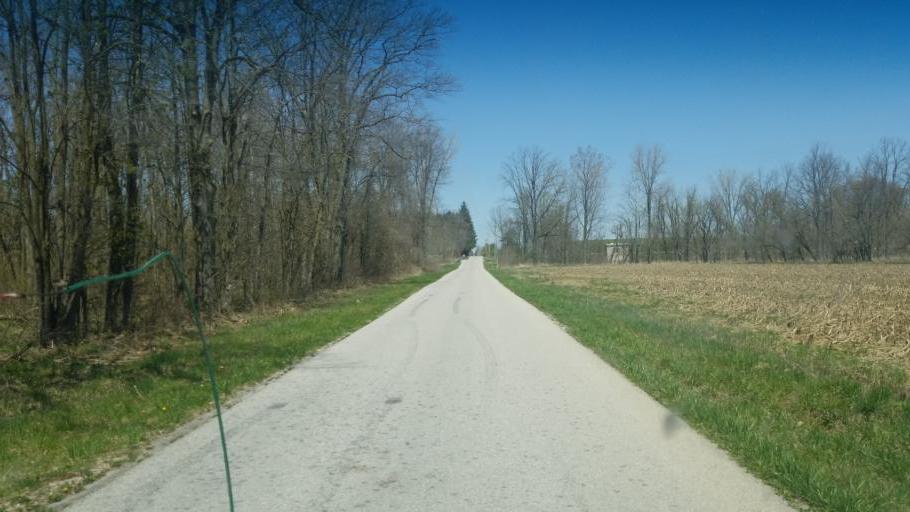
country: US
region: Ohio
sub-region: Huron County
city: New London
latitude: 41.0621
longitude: -82.4367
